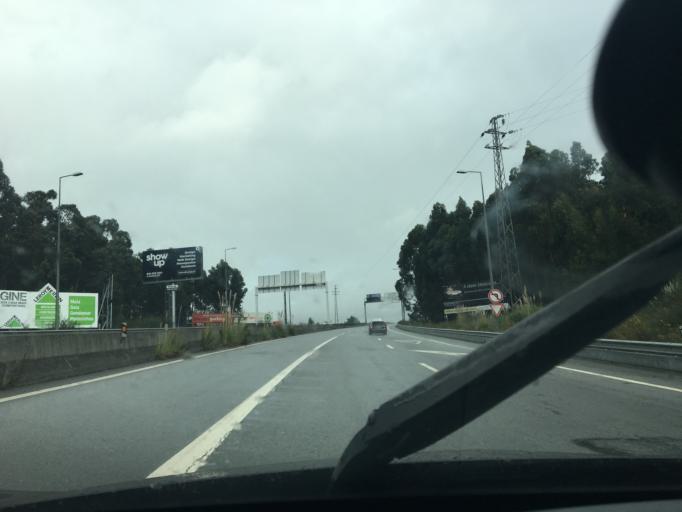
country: PT
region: Porto
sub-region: Matosinhos
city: Santa Cruz do Bispo
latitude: 41.2299
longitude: -8.6680
